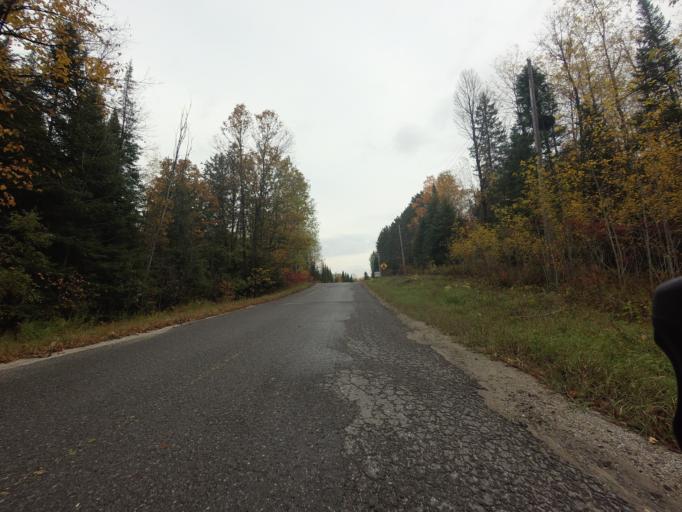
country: CA
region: Ontario
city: Perth
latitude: 45.1195
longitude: -76.4974
